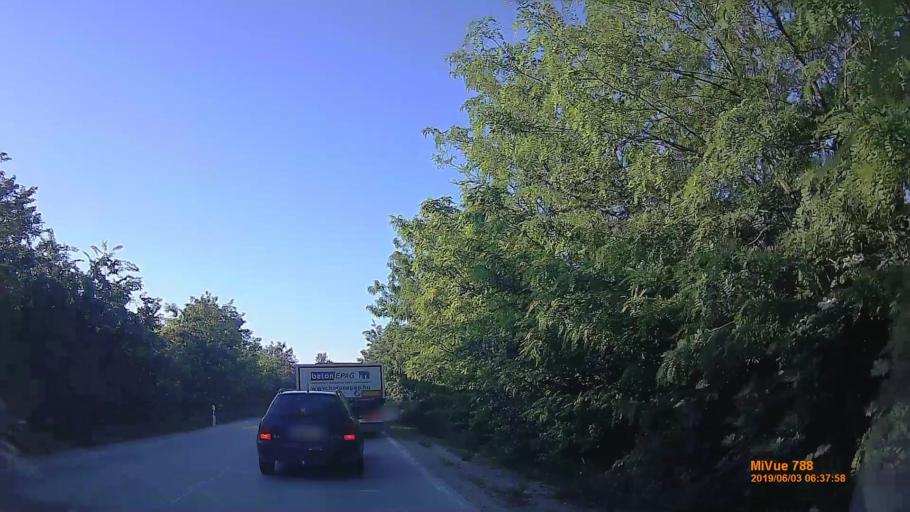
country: HU
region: Pest
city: Dunavarsany
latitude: 47.2963
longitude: 19.0923
